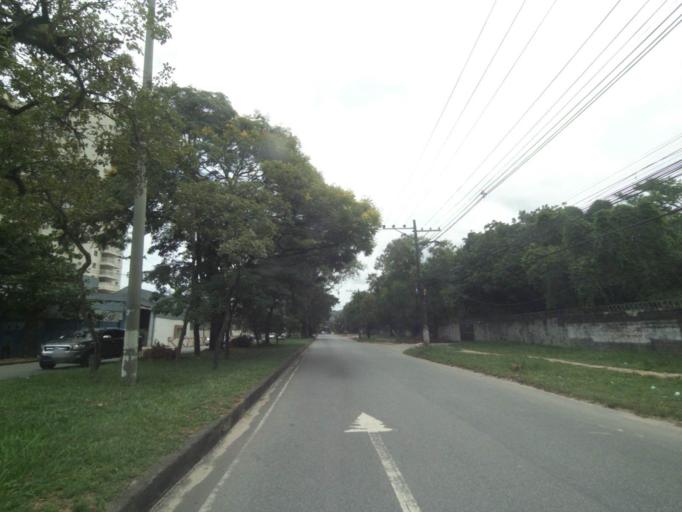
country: BR
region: Rio de Janeiro
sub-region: Nilopolis
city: Nilopolis
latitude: -22.9628
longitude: -43.4012
